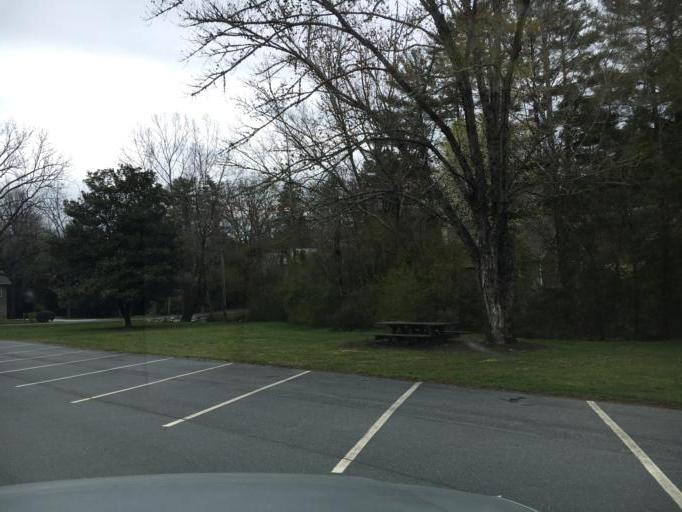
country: US
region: North Carolina
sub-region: Transylvania County
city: Brevard
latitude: 35.2239
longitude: -82.7291
